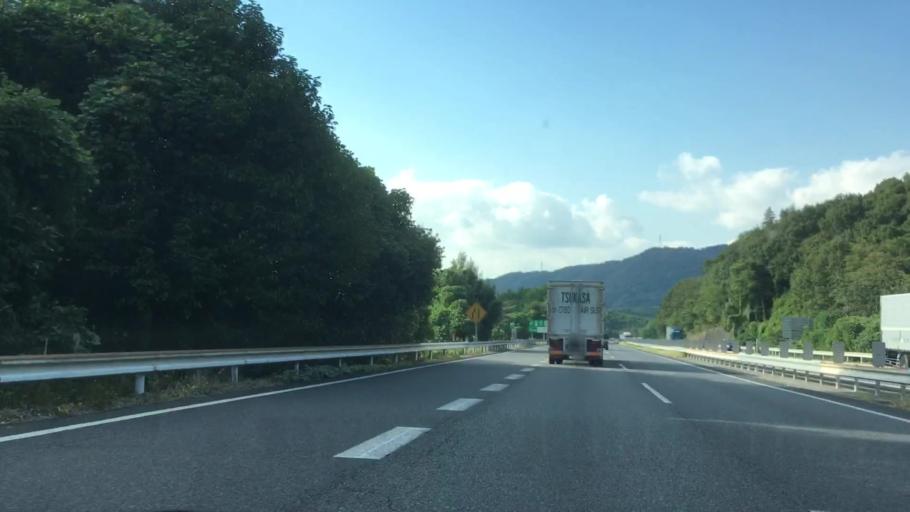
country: JP
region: Yamaguchi
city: Kudamatsu
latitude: 34.0352
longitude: 131.9283
